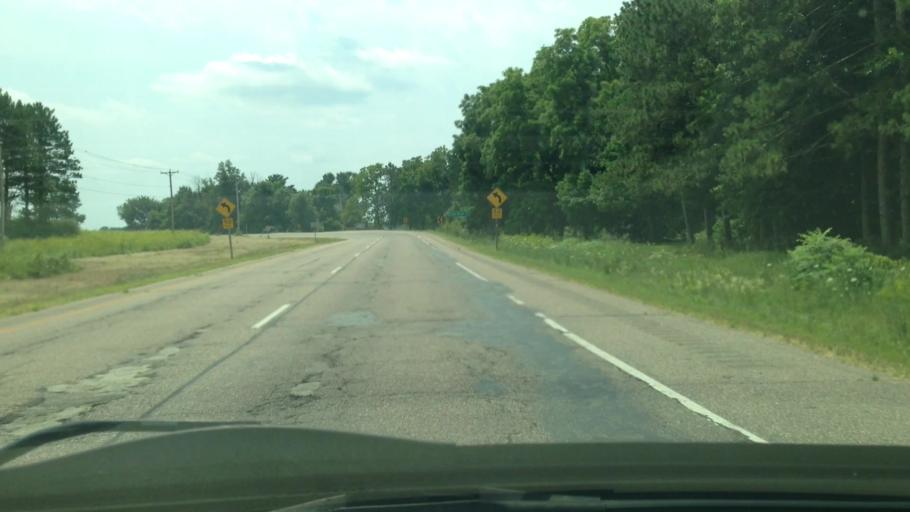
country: US
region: Wisconsin
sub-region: Sauk County
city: Prairie du Sac
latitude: 43.3538
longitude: -89.7685
